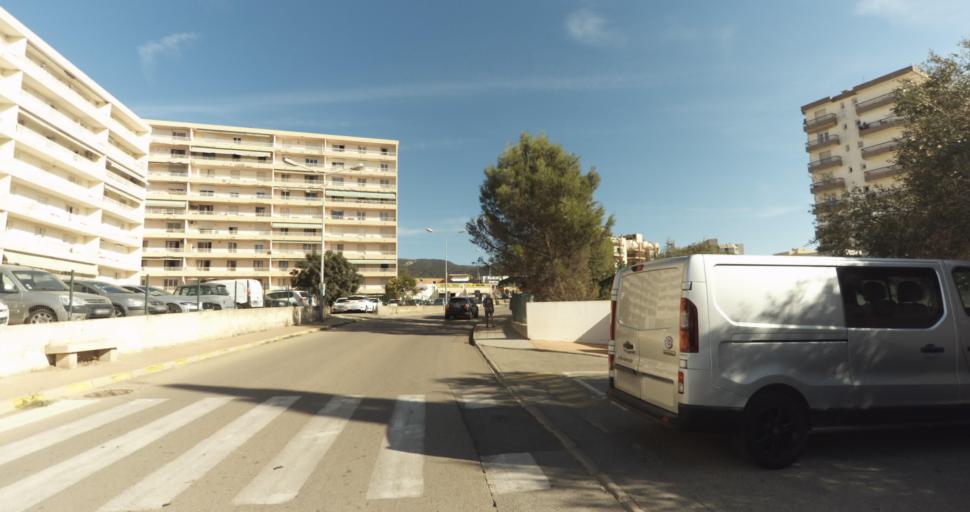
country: FR
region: Corsica
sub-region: Departement de la Corse-du-Sud
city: Ajaccio
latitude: 41.9396
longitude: 8.7457
